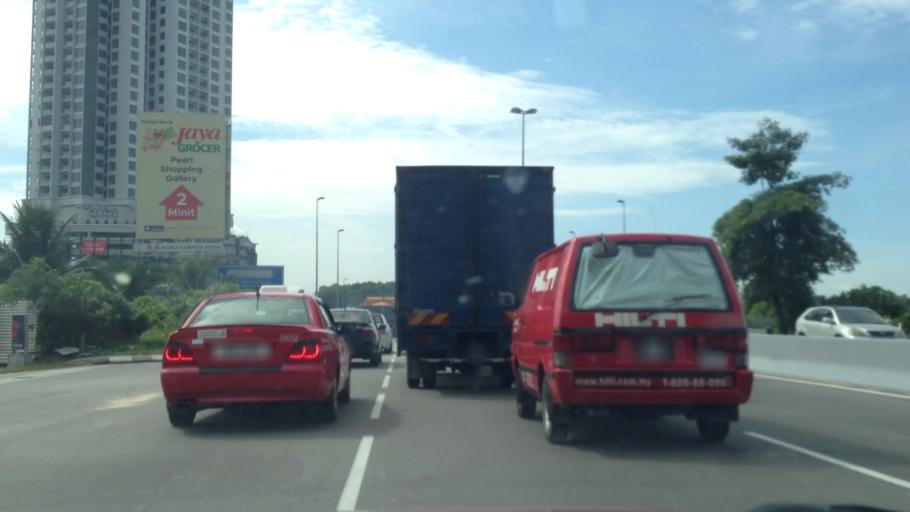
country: MY
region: Selangor
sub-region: Petaling
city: Petaling Jaya
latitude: 3.0830
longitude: 101.6633
